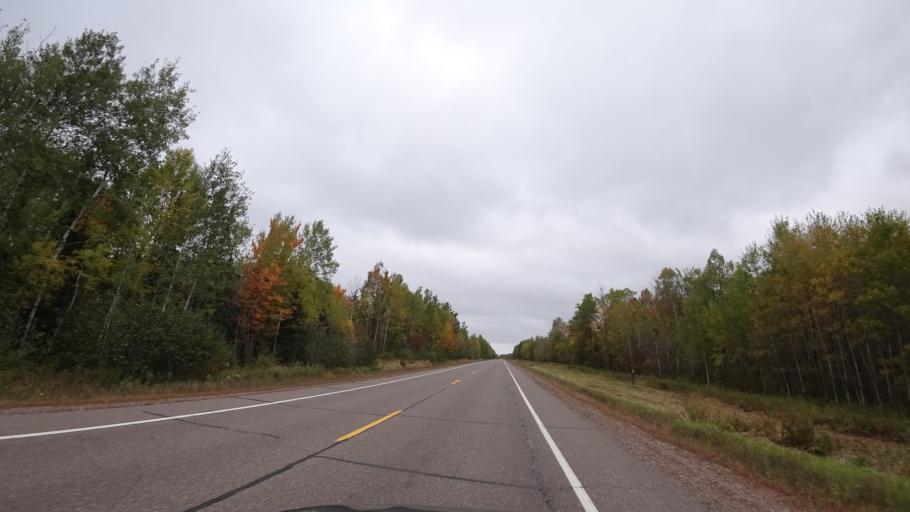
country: US
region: Wisconsin
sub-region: Rusk County
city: Ladysmith
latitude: 45.5574
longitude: -91.1117
